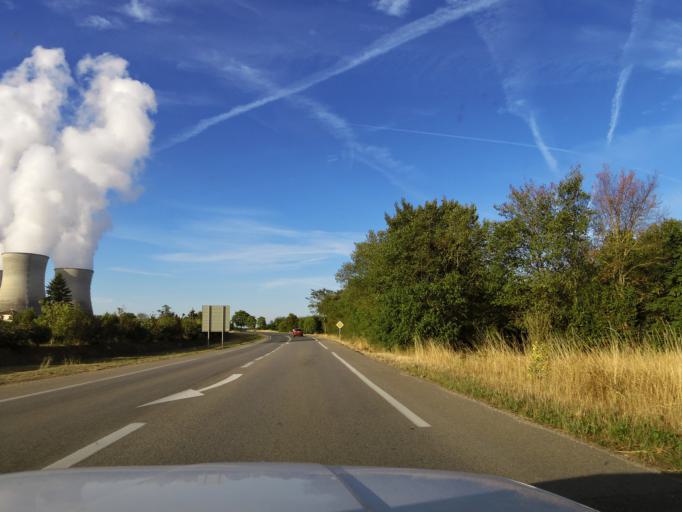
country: FR
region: Rhone-Alpes
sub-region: Departement de l'Isere
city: Hieres-sur-Amby
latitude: 45.8115
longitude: 5.2711
